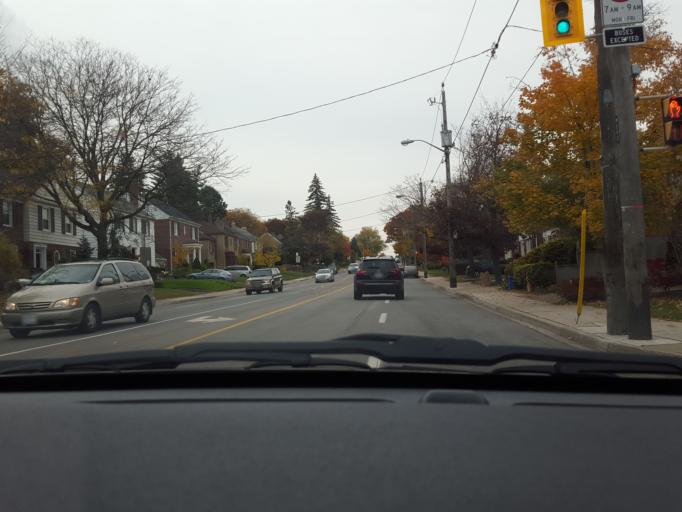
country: CA
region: Ontario
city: Willowdale
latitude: 43.7284
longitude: -79.3866
